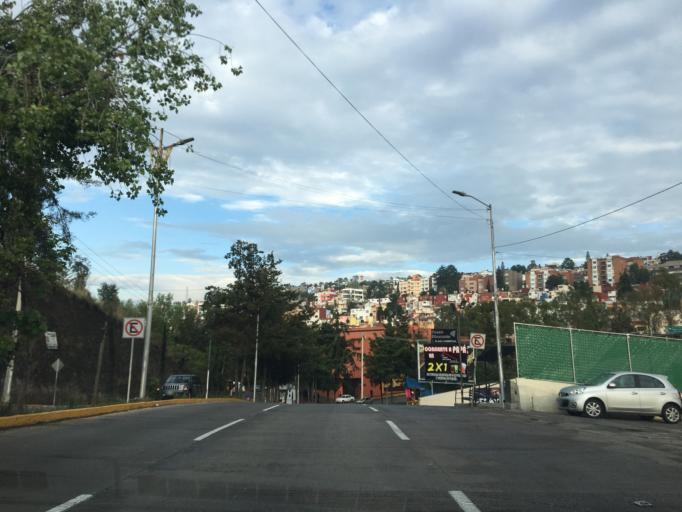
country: MX
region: Mexico
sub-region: Naucalpan de Juarez
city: Rincon Verde
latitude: 19.5174
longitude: -99.2703
